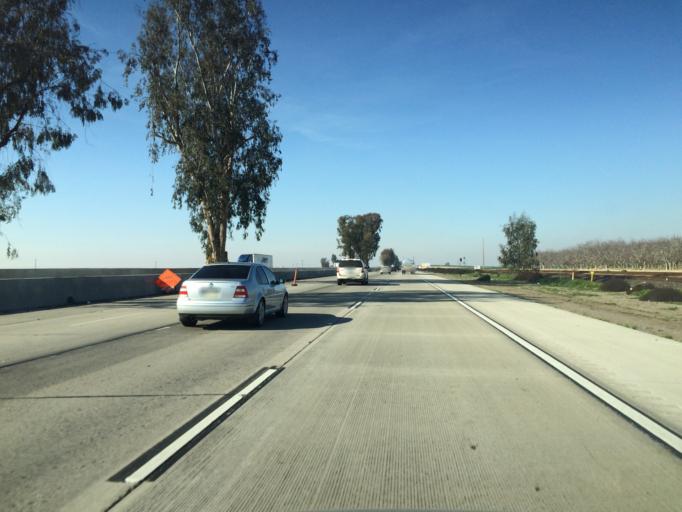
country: US
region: California
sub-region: Tulare County
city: Goshen
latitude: 36.3723
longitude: -119.4351
